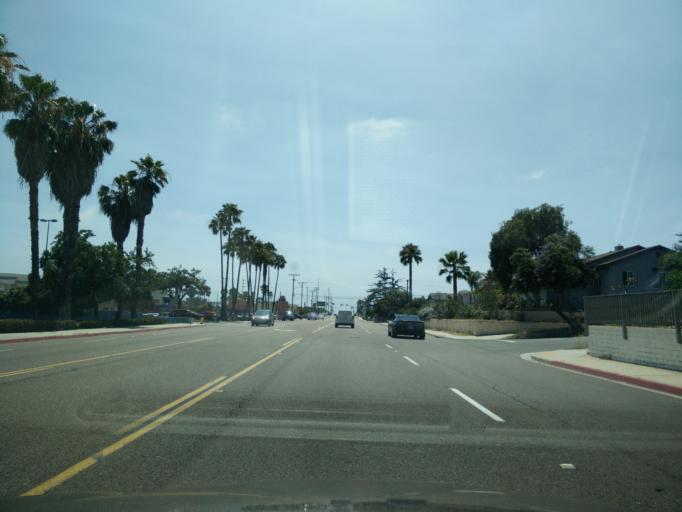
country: US
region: California
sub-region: San Diego County
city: Chula Vista
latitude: 32.6602
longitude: -117.0879
